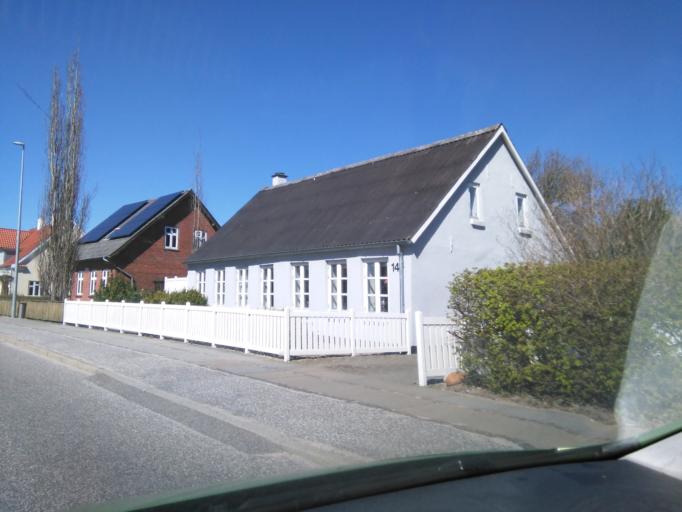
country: DK
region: South Denmark
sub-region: Varde Kommune
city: Varde
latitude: 55.6245
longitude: 8.4726
